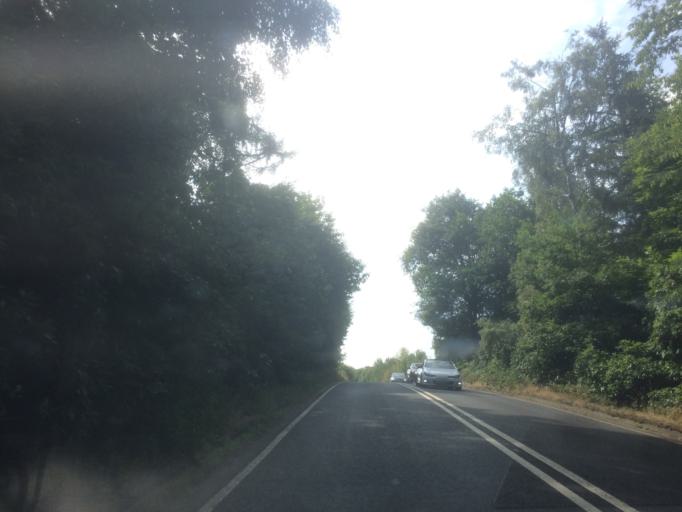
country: GB
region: England
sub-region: Buckinghamshire
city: Farnham Royal
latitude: 51.5772
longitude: -0.6245
